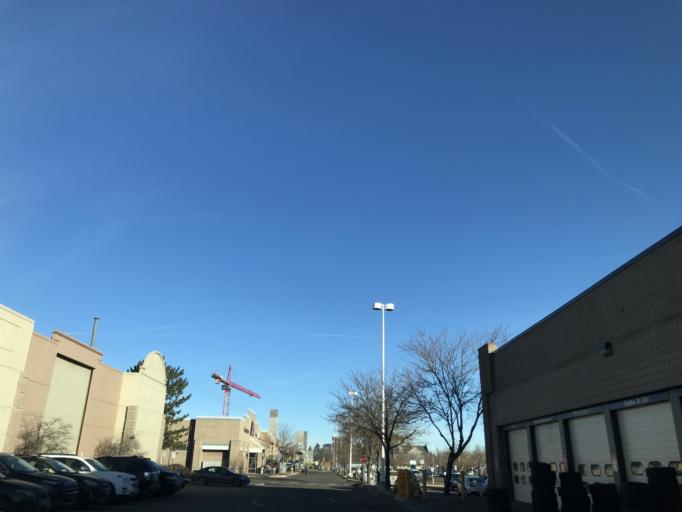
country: US
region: Colorado
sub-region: Denver County
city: Denver
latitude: 39.7078
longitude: -104.9912
